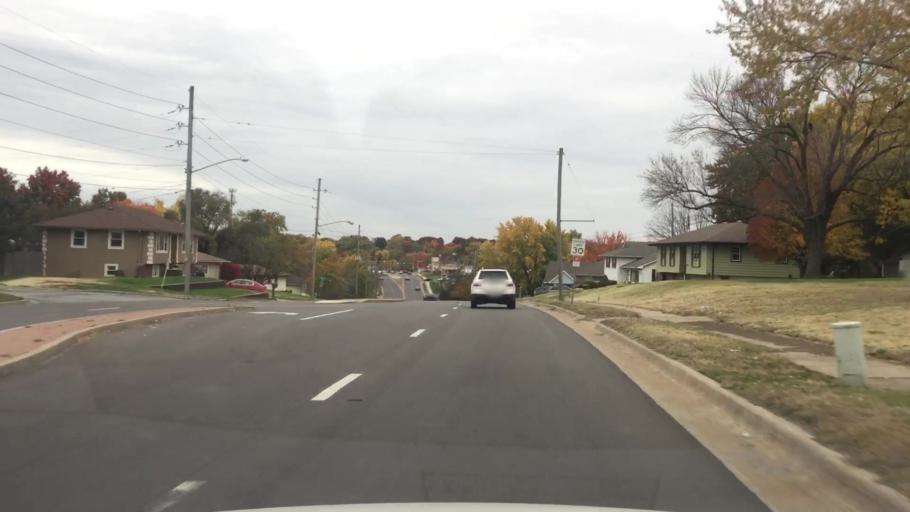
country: US
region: Kansas
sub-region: Johnson County
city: Merriam
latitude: 39.0525
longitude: -94.6815
